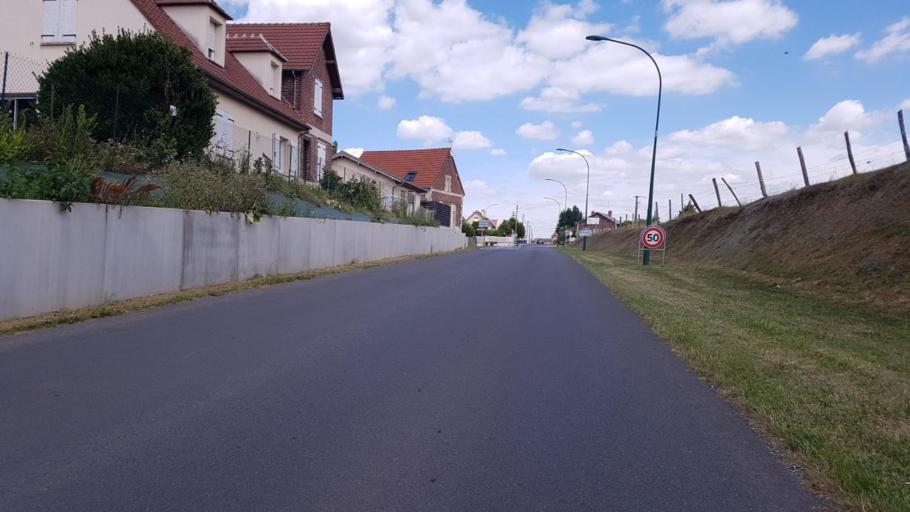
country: FR
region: Picardie
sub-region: Departement de l'Oise
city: Tracy-le-Mont
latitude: 49.4941
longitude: 2.9674
